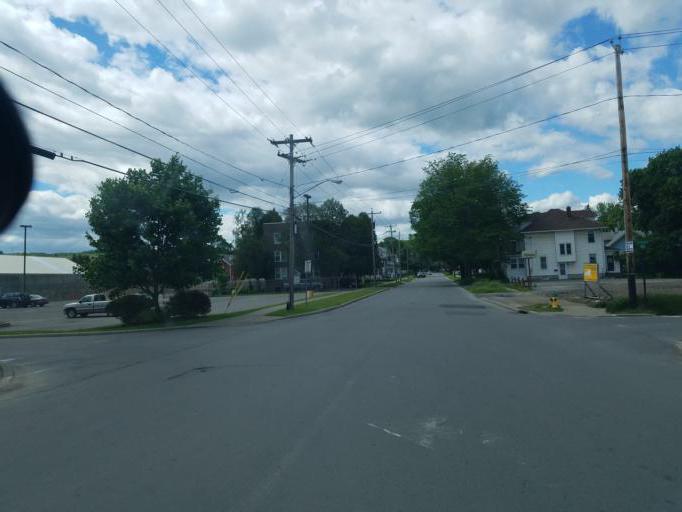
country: US
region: New York
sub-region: Herkimer County
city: Herkimer
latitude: 43.0229
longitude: -74.9932
